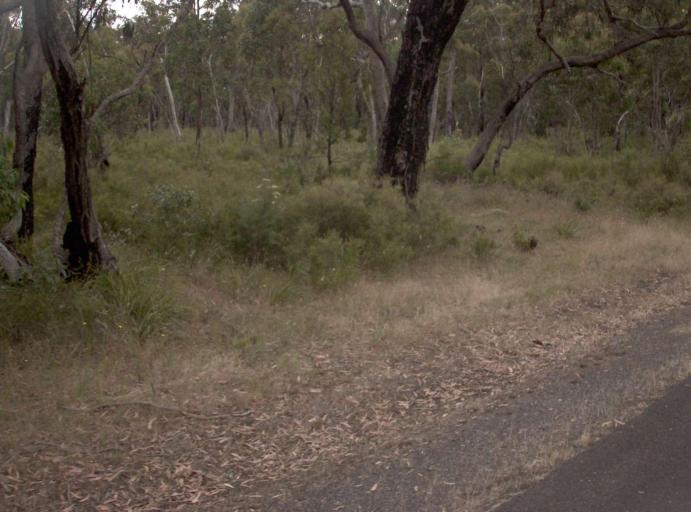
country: AU
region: Victoria
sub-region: Wellington
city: Sale
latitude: -38.3958
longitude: 146.9723
